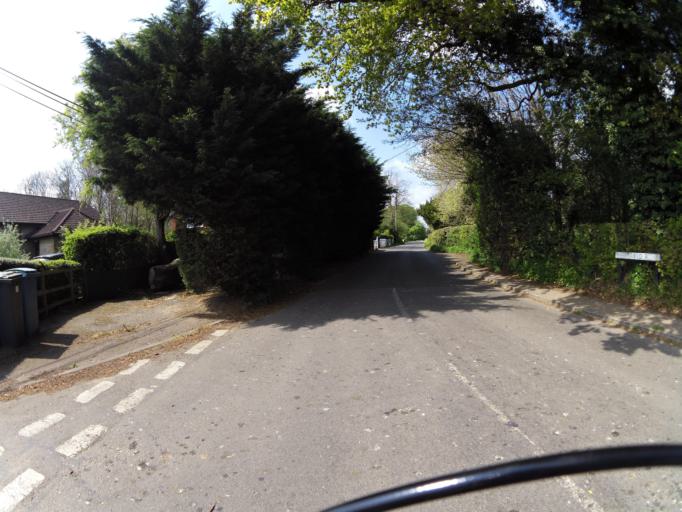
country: GB
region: England
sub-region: Suffolk
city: Hadleigh
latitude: 52.0797
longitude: 0.9982
